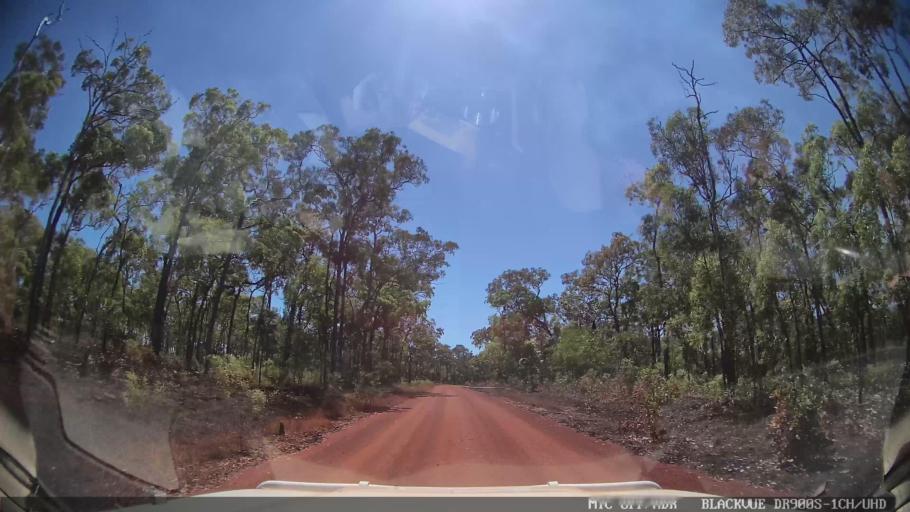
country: AU
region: Queensland
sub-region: Torres
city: Thursday Island
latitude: -10.9732
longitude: 142.3403
